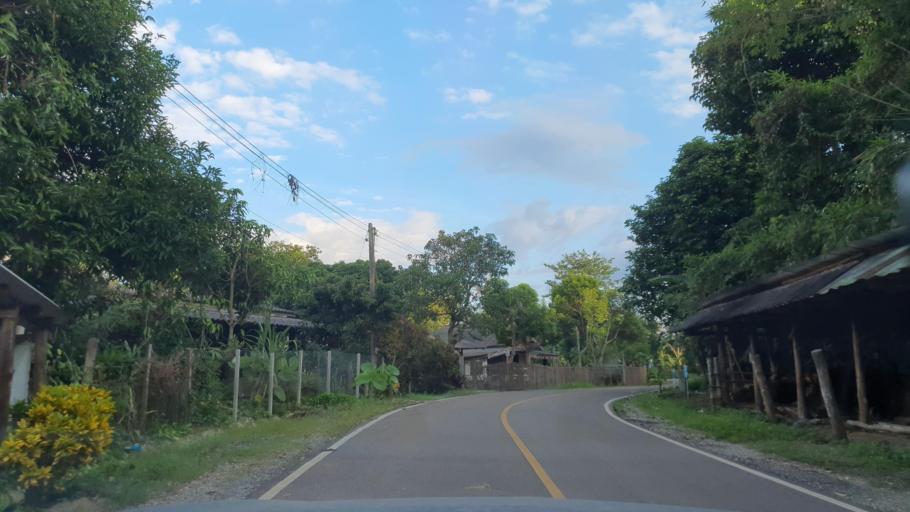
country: TH
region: Chiang Mai
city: Mae On
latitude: 18.8660
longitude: 99.2413
